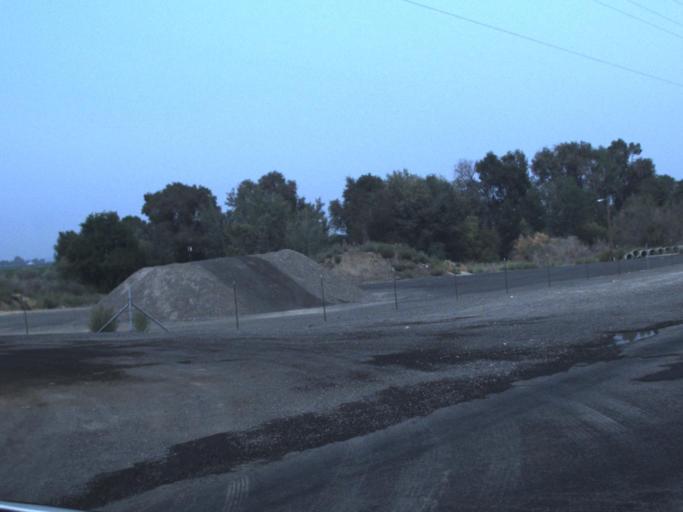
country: US
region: Washington
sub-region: Yakima County
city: Sunnyside
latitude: 46.3498
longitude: -119.9791
